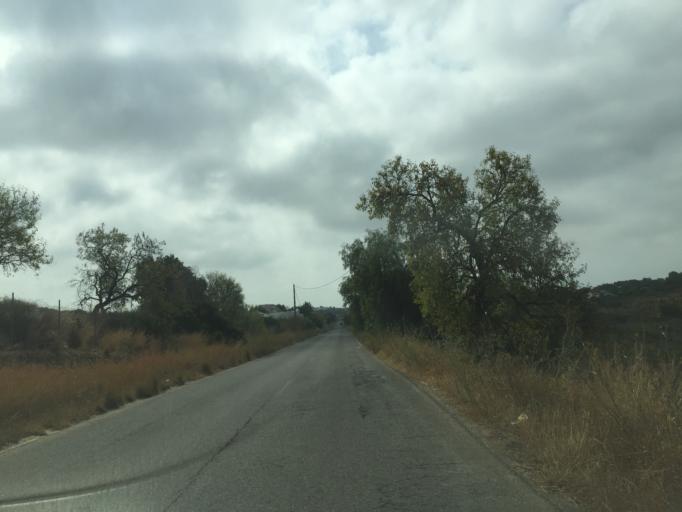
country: PT
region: Faro
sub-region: Olhao
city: Olhao
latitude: 37.0698
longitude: -7.8825
